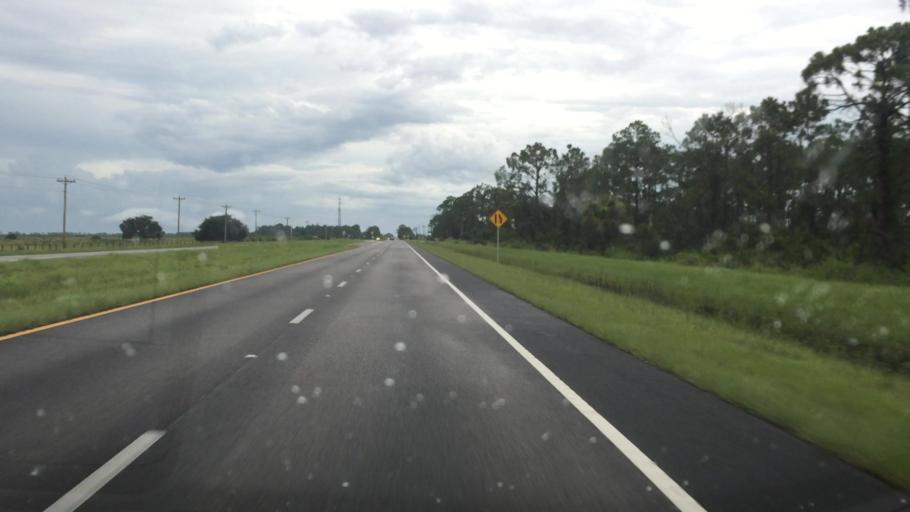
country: US
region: Florida
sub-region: Lee County
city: Lehigh Acres
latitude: 26.5149
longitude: -81.5503
